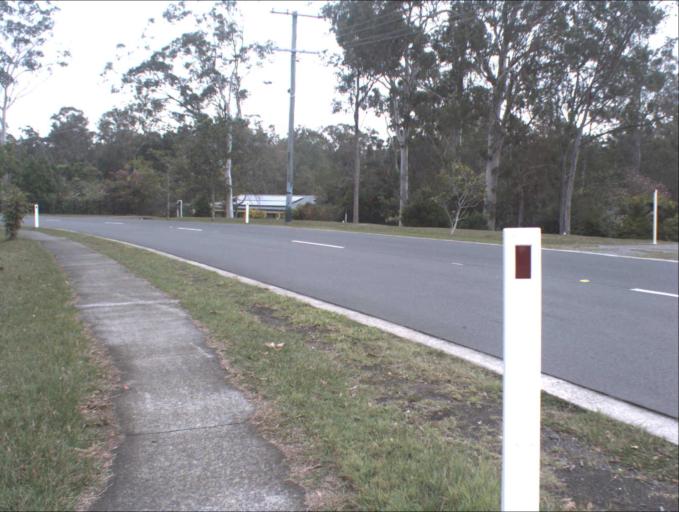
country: AU
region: Queensland
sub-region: Brisbane
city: Forest Lake
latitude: -27.6665
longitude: 152.9976
